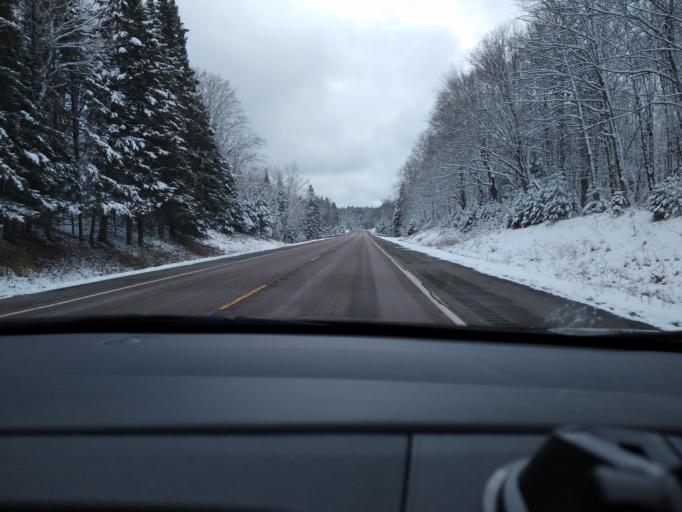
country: US
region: Wisconsin
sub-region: Vilas County
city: Eagle River
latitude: 46.2380
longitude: -89.0891
